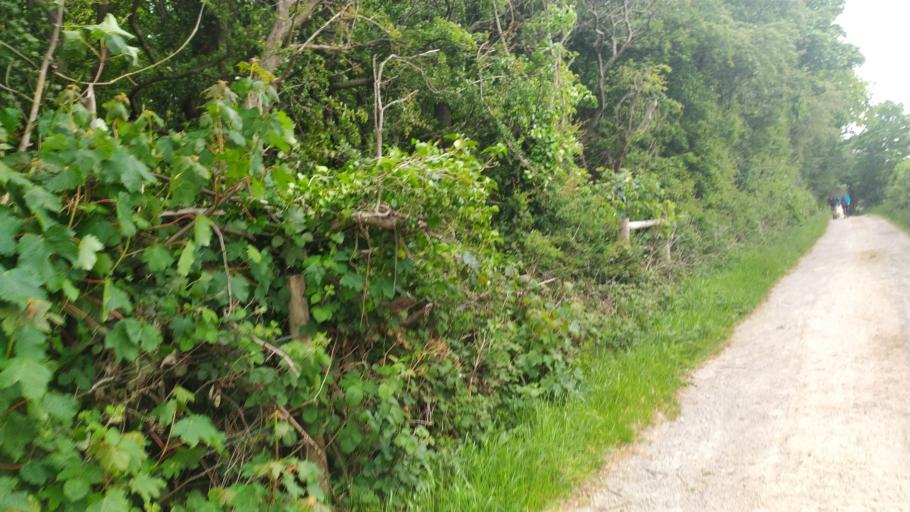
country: GB
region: England
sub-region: City and Borough of Leeds
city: Thorner
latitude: 53.8581
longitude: -1.3909
